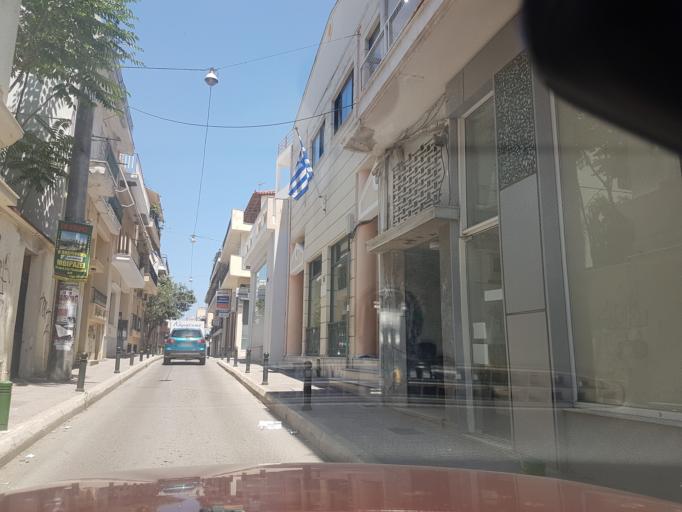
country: GR
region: Central Greece
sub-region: Nomos Evvoias
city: Chalkida
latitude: 38.4619
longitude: 23.5919
